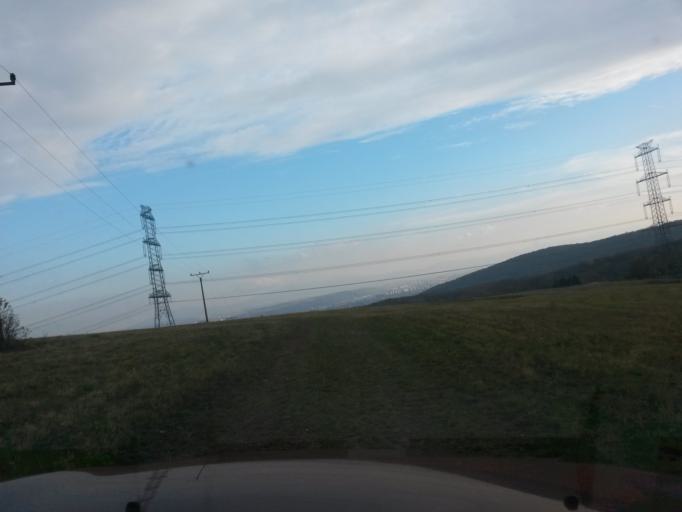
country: SK
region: Kosicky
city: Kosice
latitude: 48.7651
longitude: 21.2157
